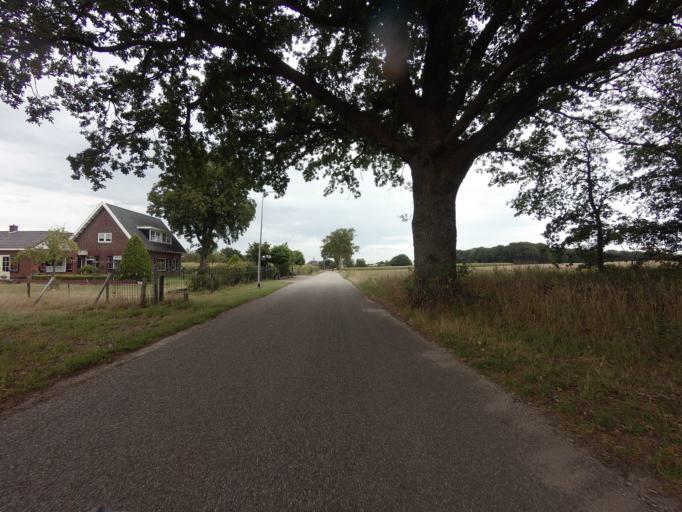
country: NL
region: Overijssel
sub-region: Gemeente Raalte
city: Raalte
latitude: 52.3548
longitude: 6.3835
